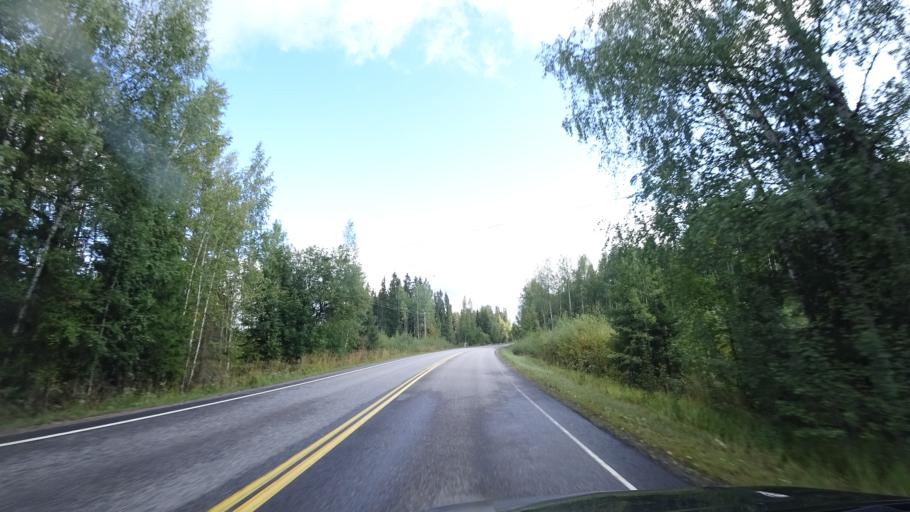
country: FI
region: Uusimaa
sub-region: Helsinki
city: Hyvinge
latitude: 60.5378
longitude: 24.9244
